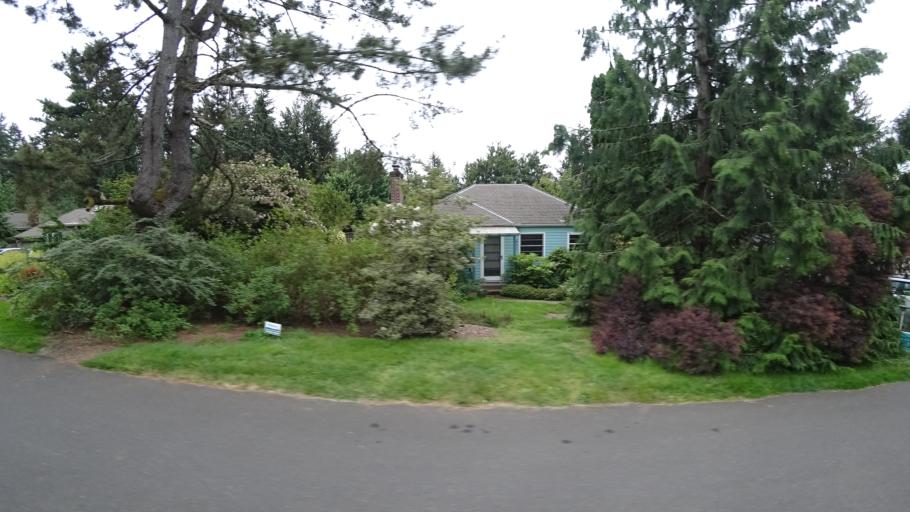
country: US
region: Oregon
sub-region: Multnomah County
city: Portland
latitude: 45.4859
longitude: -122.7019
